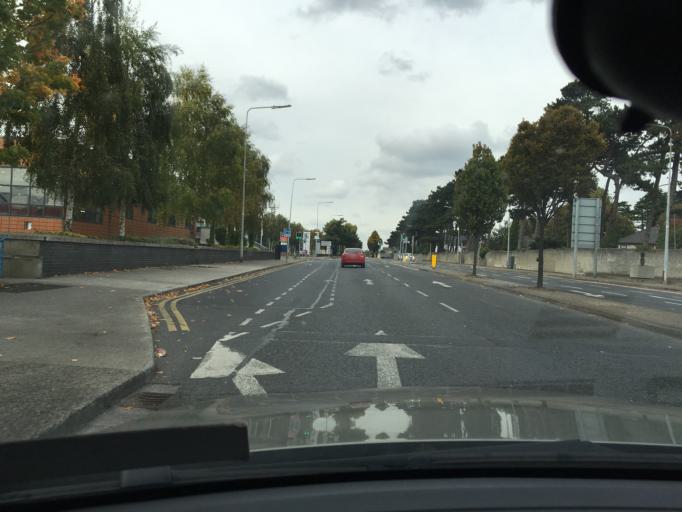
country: IE
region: Leinster
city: Cabra
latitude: 53.3617
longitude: -6.2988
